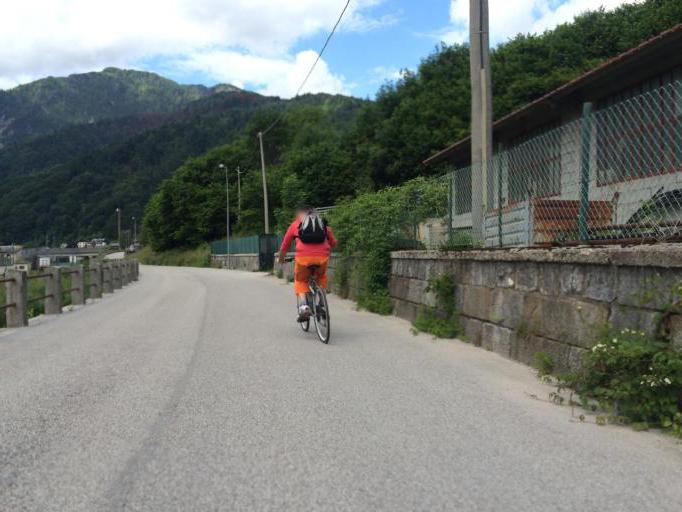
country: IT
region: Friuli Venezia Giulia
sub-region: Provincia di Udine
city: Pontebba
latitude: 46.5094
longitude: 13.3099
